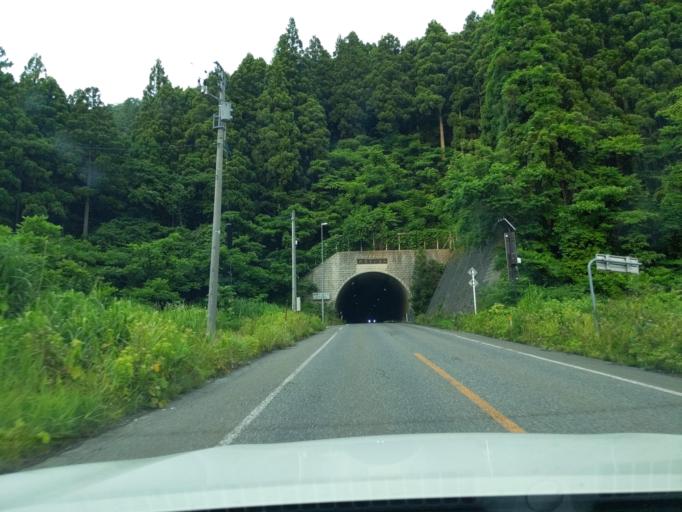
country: JP
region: Niigata
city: Nagaoka
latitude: 37.4459
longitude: 138.6905
